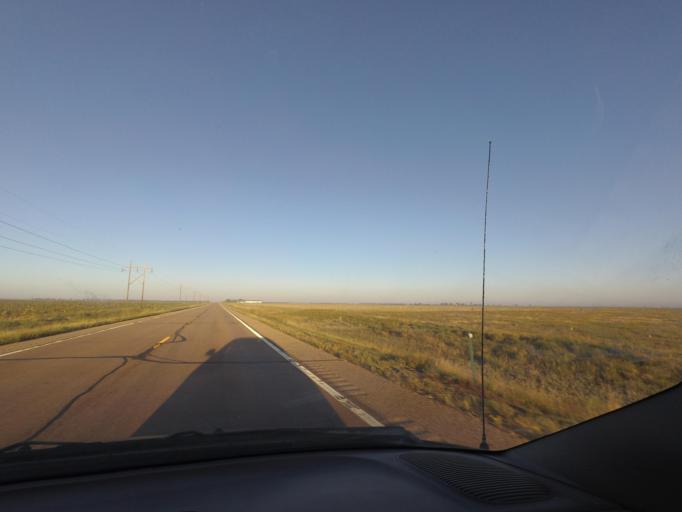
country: US
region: Colorado
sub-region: Yuma County
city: Yuma
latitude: 39.6559
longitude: -102.7341
